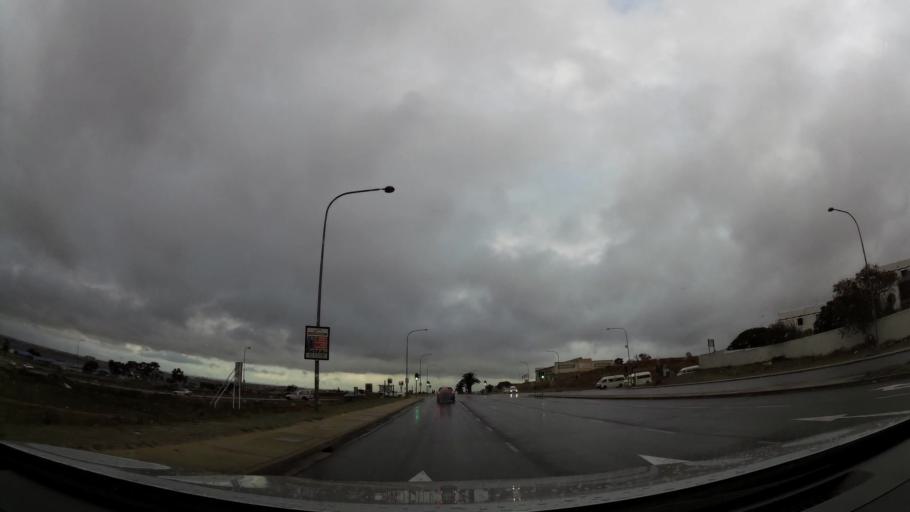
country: ZA
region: Eastern Cape
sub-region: Nelson Mandela Bay Metropolitan Municipality
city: Port Elizabeth
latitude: -33.8916
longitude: 25.5237
